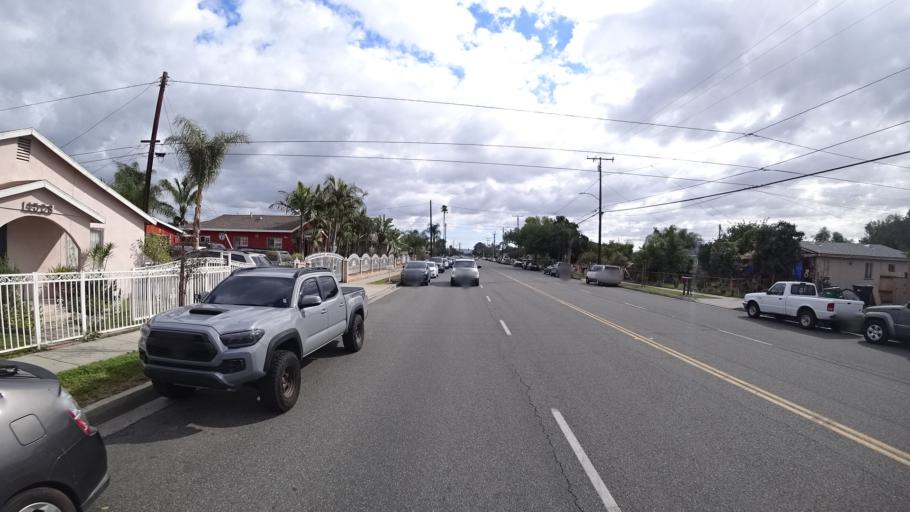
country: US
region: California
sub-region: Los Angeles County
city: Baldwin Park
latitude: 34.0946
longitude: -117.9736
